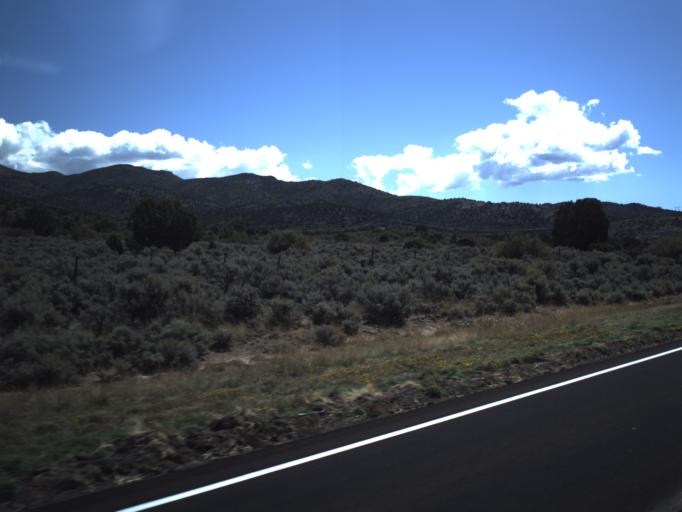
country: US
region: Utah
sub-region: Washington County
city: Enterprise
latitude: 37.4947
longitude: -113.6308
